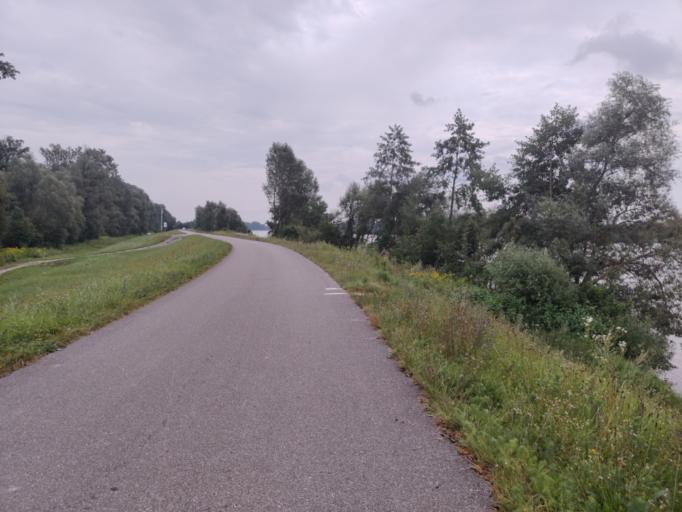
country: AT
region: Lower Austria
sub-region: Politischer Bezirk Amstetten
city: Ennsdorf
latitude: 48.2308
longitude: 14.5665
